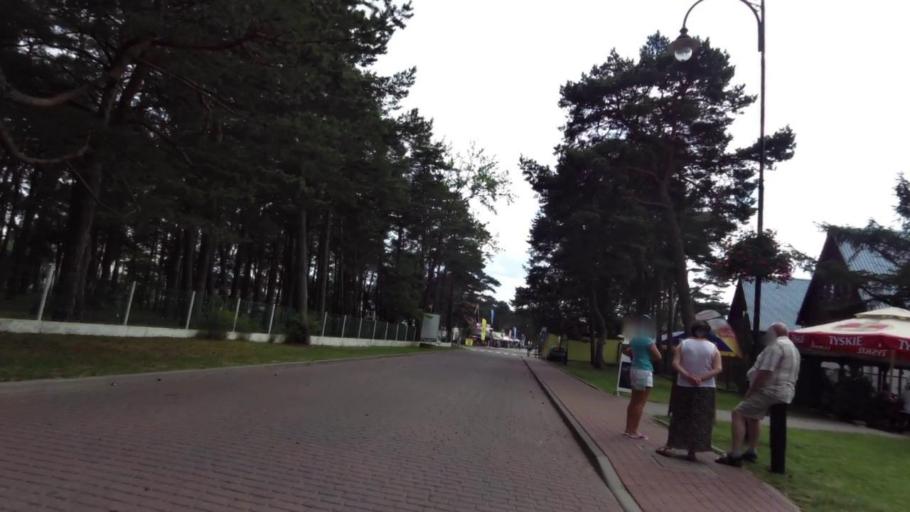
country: PL
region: West Pomeranian Voivodeship
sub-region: Powiat gryficki
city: Mrzezyno
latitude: 54.1454
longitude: 15.3022
